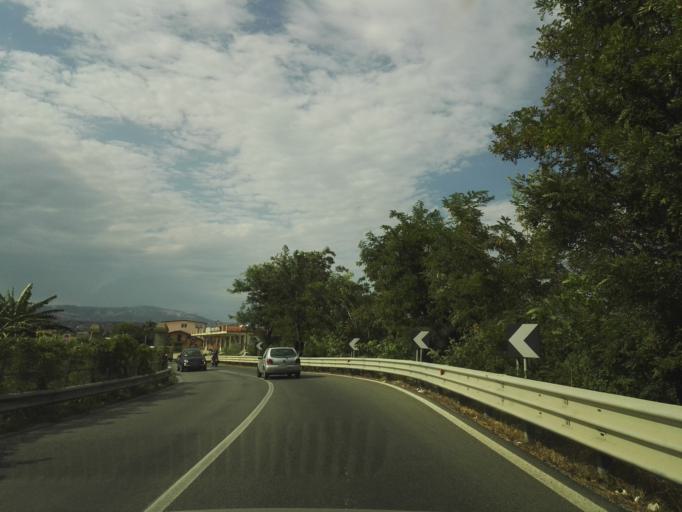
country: IT
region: Calabria
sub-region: Provincia di Catanzaro
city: Marina di Davoli
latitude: 38.6559
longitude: 16.5476
